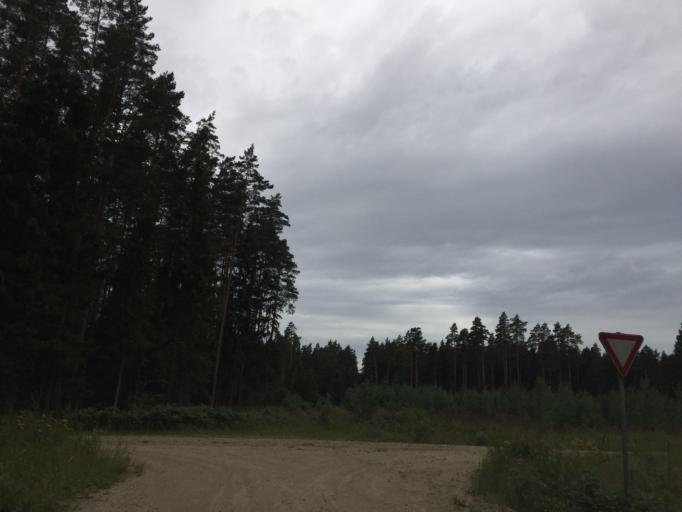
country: LV
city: Tireli
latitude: 56.8324
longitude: 23.6322
